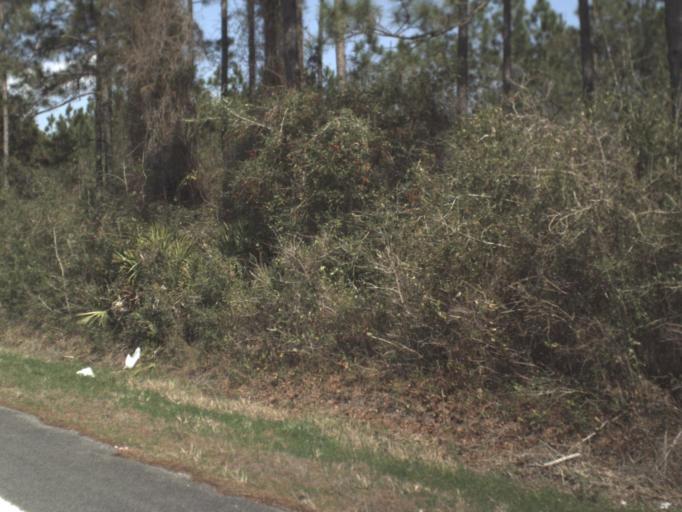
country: US
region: Florida
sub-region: Franklin County
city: Carrabelle
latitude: 29.9580
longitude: -84.5043
